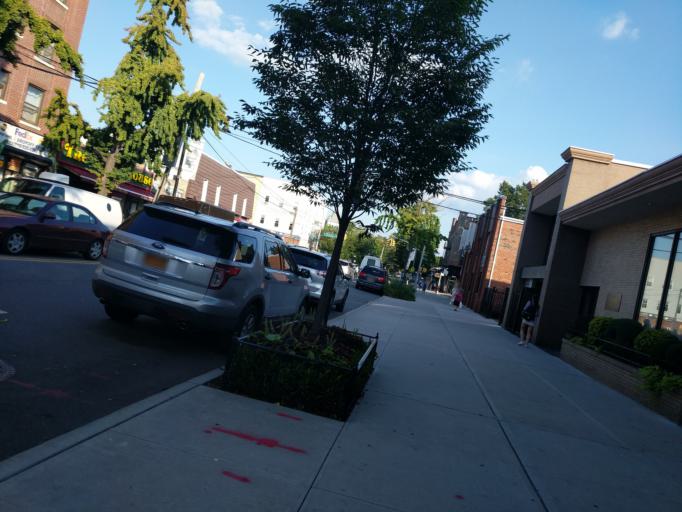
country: US
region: New York
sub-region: Queens County
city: Long Island City
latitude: 40.7732
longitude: -73.9067
